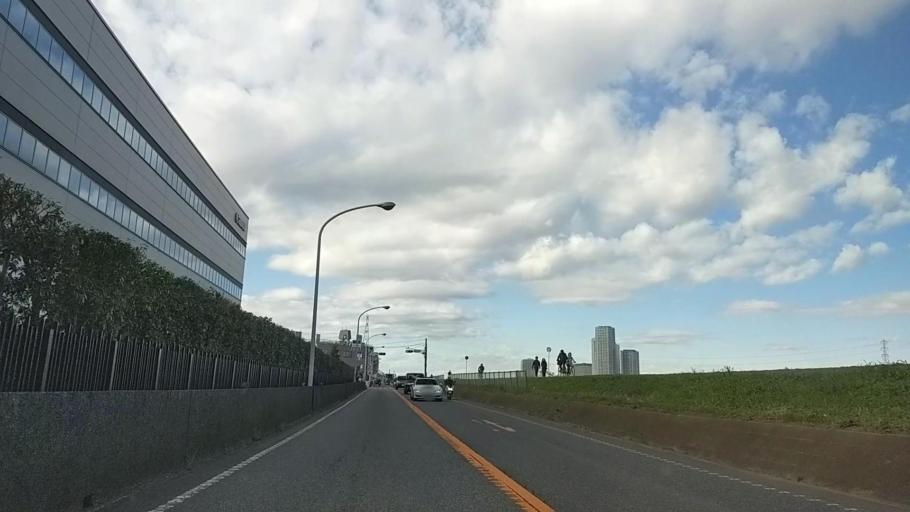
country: JP
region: Tokyo
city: Tokyo
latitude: 35.5963
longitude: 139.6415
